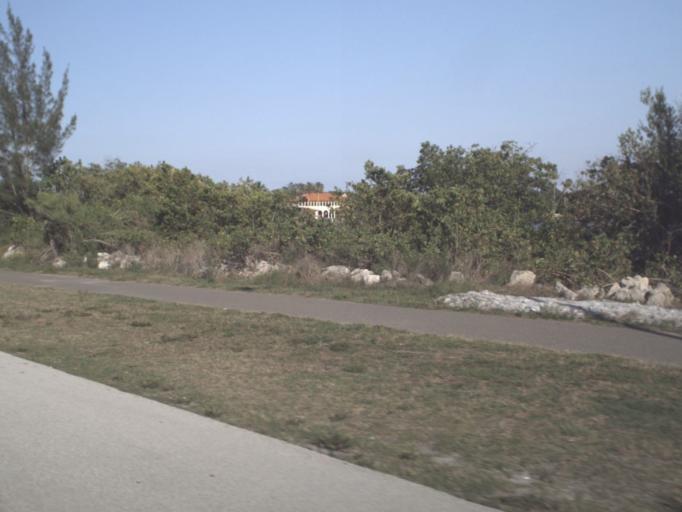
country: US
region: Florida
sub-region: Brevard County
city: Indialantic
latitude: 28.0881
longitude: -80.5788
